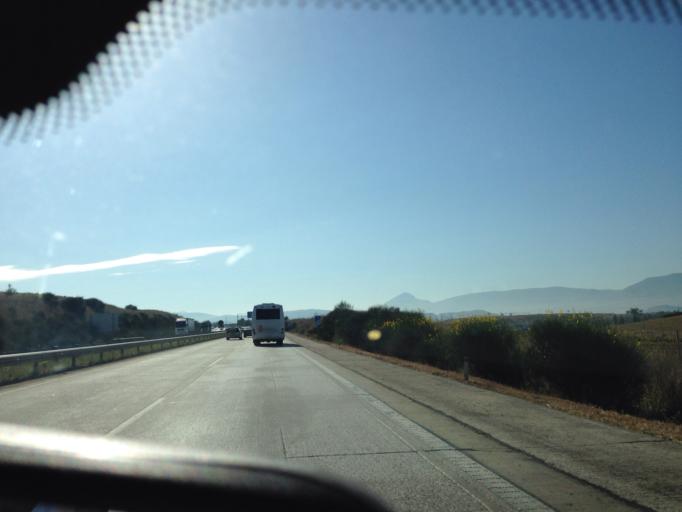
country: ES
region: Navarre
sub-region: Provincia de Navarra
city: Iturrama
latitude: 42.7887
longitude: -1.6619
